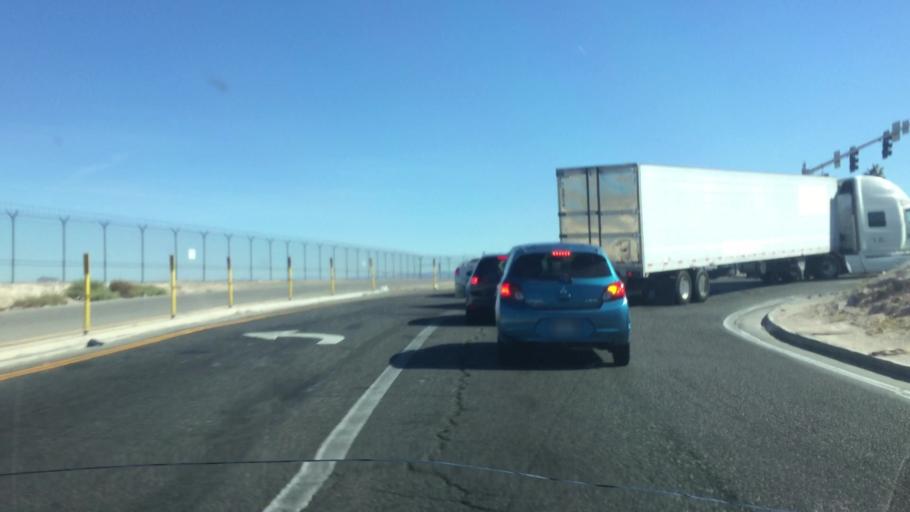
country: US
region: Nevada
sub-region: Clark County
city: Paradise
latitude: 36.0720
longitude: -115.1416
